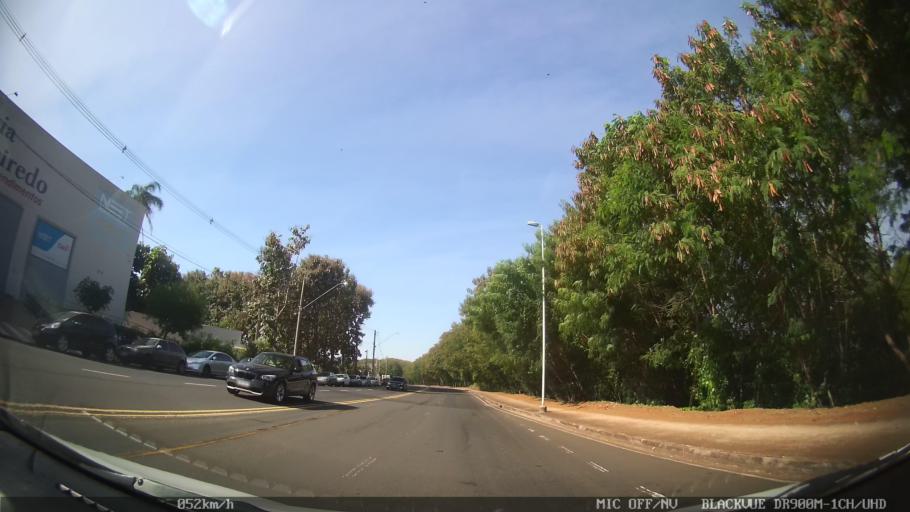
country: BR
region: Sao Paulo
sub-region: Sao Jose Do Rio Preto
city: Sao Jose do Rio Preto
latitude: -20.8008
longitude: -49.4050
